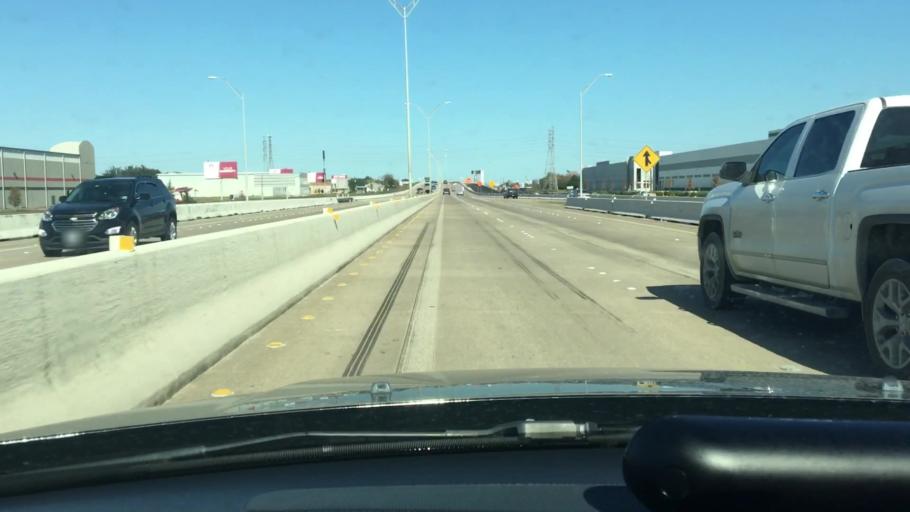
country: US
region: Texas
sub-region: Harris County
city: Deer Park
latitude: 29.6959
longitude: -95.1535
